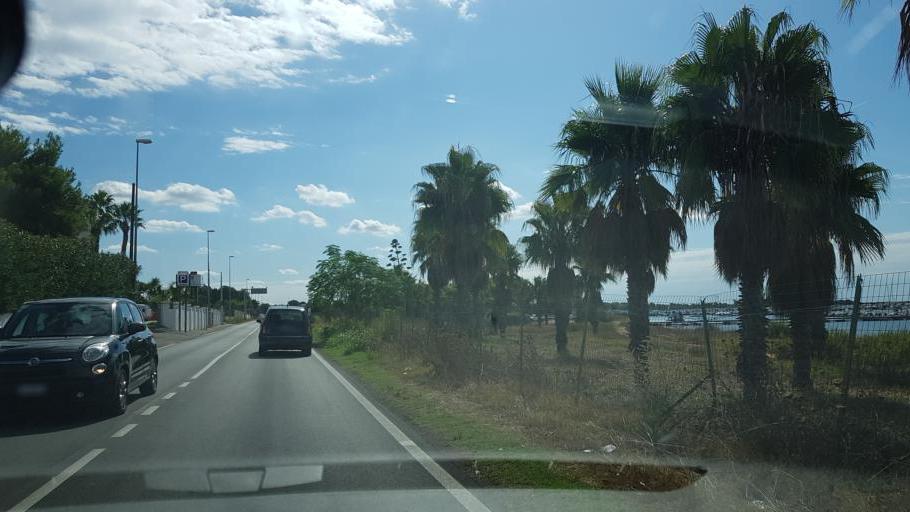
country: IT
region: Apulia
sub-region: Provincia di Lecce
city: Porto Cesareo
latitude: 40.2536
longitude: 17.9070
